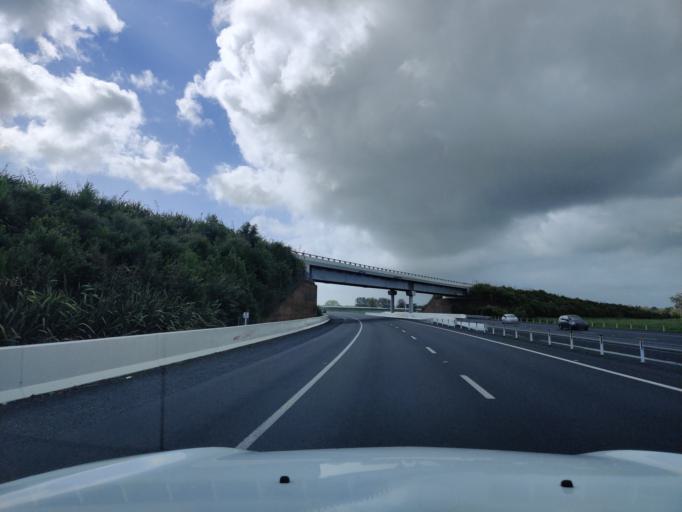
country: NZ
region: Waikato
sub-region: Waipa District
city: Cambridge
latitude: -37.8664
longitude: 175.4045
